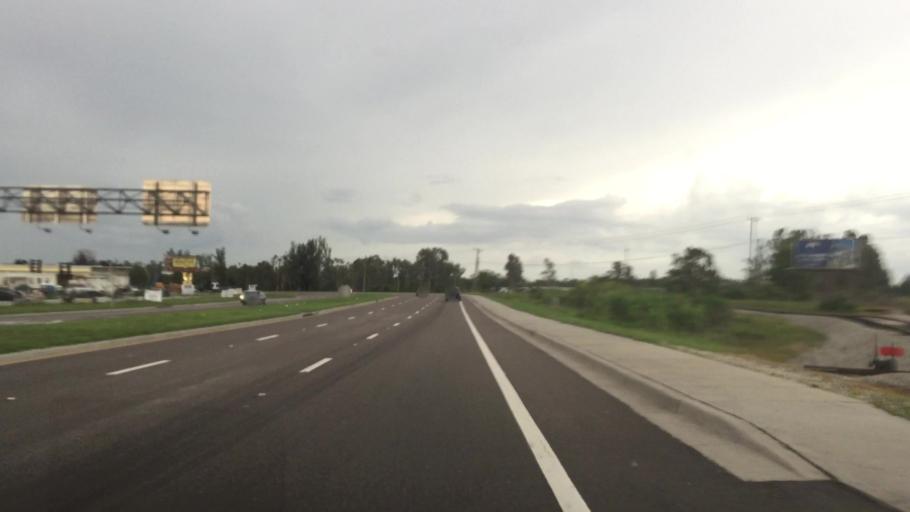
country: US
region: Florida
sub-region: Lee County
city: San Carlos Park
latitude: 26.4935
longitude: -81.8416
